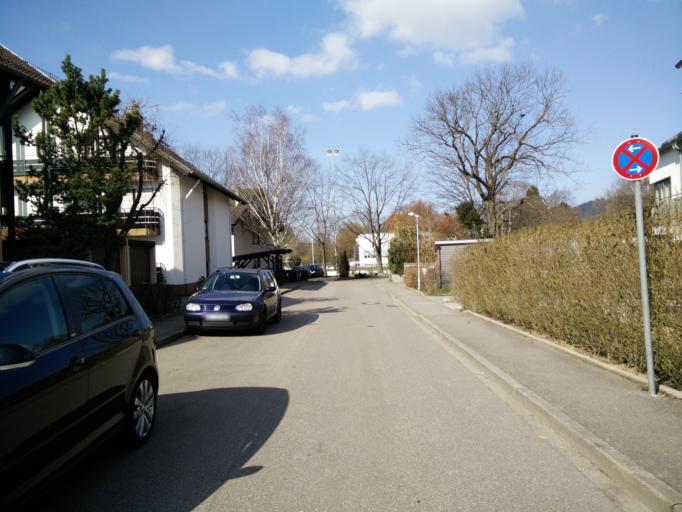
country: DE
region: Baden-Wuerttemberg
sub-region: Freiburg Region
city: Kirchzarten
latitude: 47.9839
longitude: 7.9060
